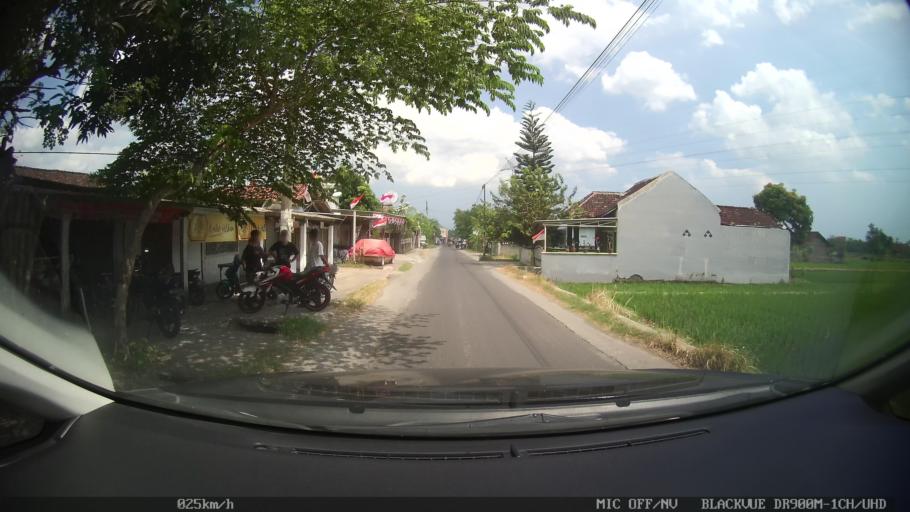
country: ID
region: Daerah Istimewa Yogyakarta
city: Kasihan
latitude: -7.8179
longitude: 110.3431
